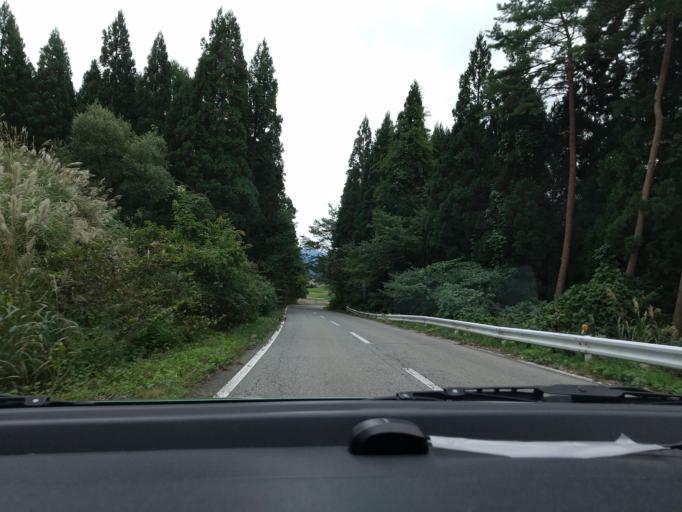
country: JP
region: Akita
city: Kakunodatemachi
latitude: 39.5485
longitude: 140.6338
